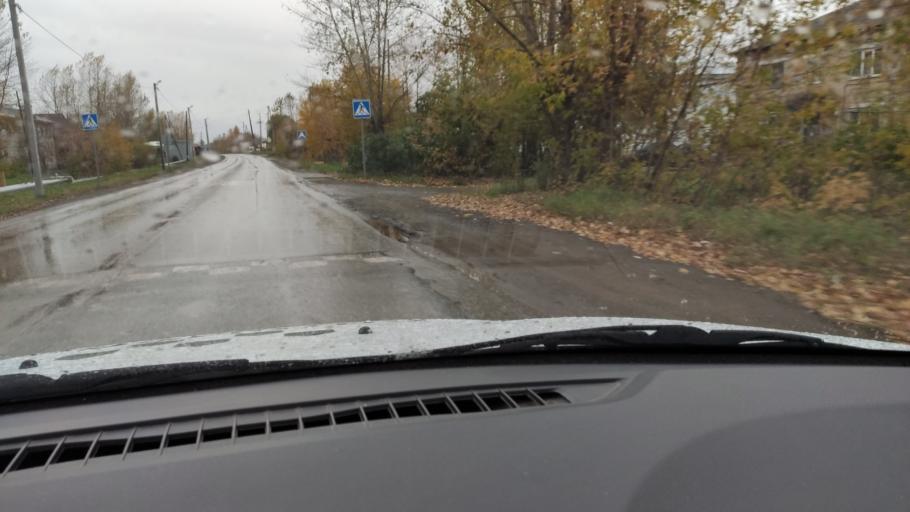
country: RU
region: Perm
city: Kondratovo
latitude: 57.9813
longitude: 56.1059
